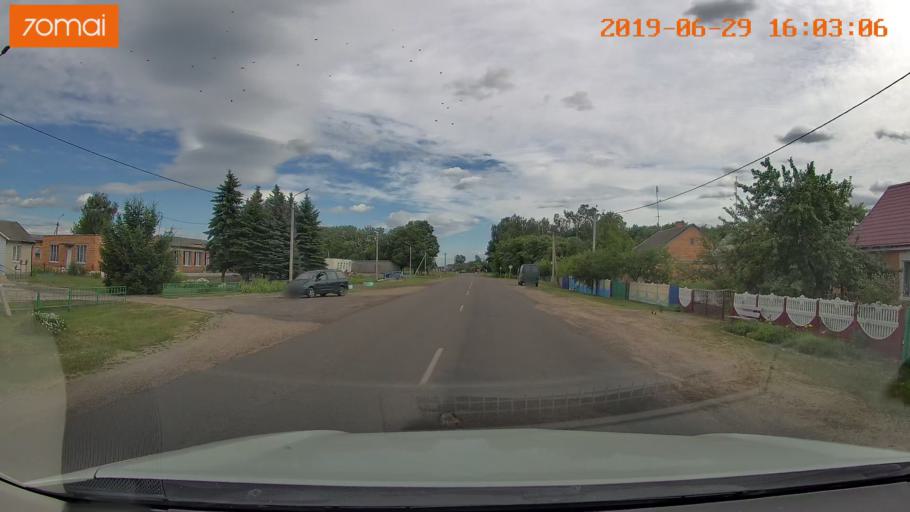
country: BY
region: Brest
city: Luninyets
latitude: 52.2309
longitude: 27.0178
